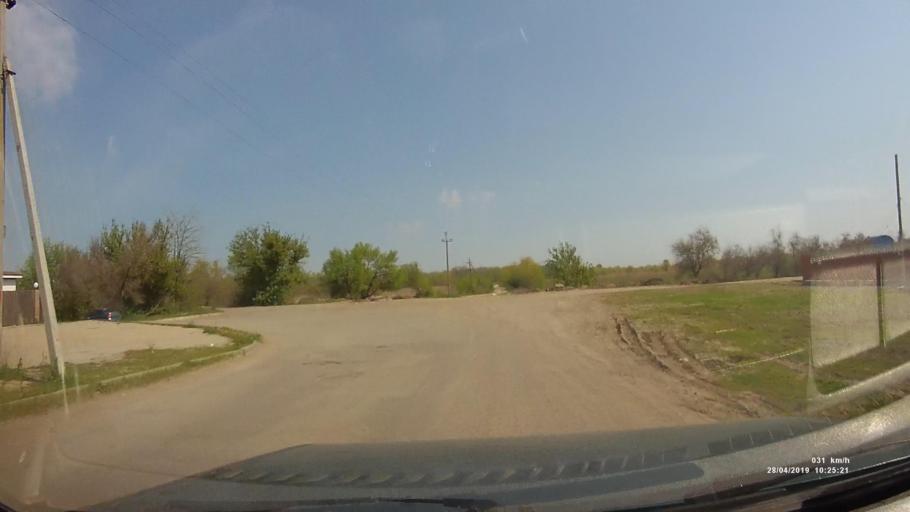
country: RU
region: Rostov
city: Azov
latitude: 47.1114
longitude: 39.4416
